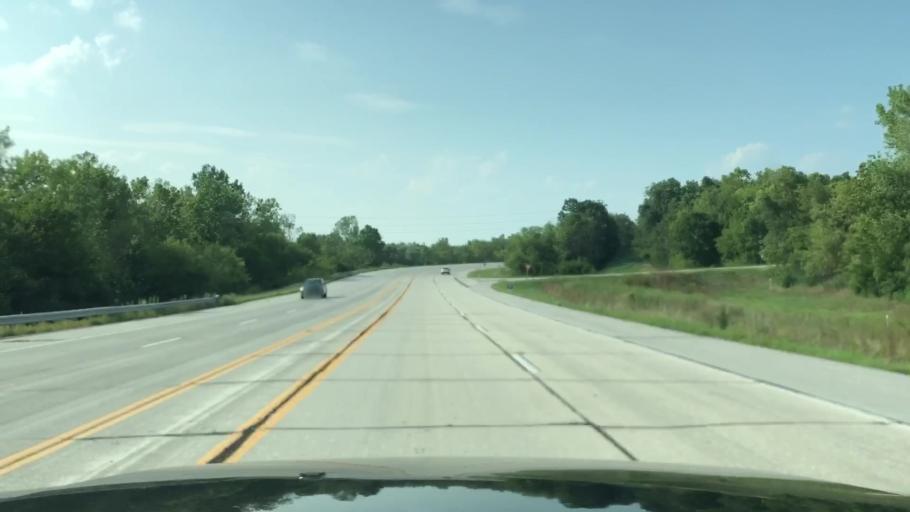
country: US
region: Missouri
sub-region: Saint Charles County
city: Lake Saint Louis
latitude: 38.8117
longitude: -90.8099
